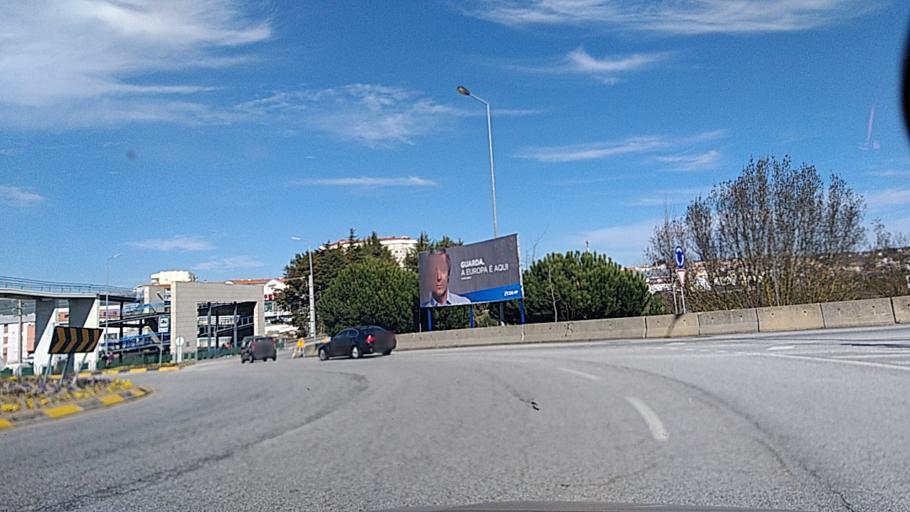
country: PT
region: Guarda
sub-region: Guarda
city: Guarda
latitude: 40.5487
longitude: -7.2484
